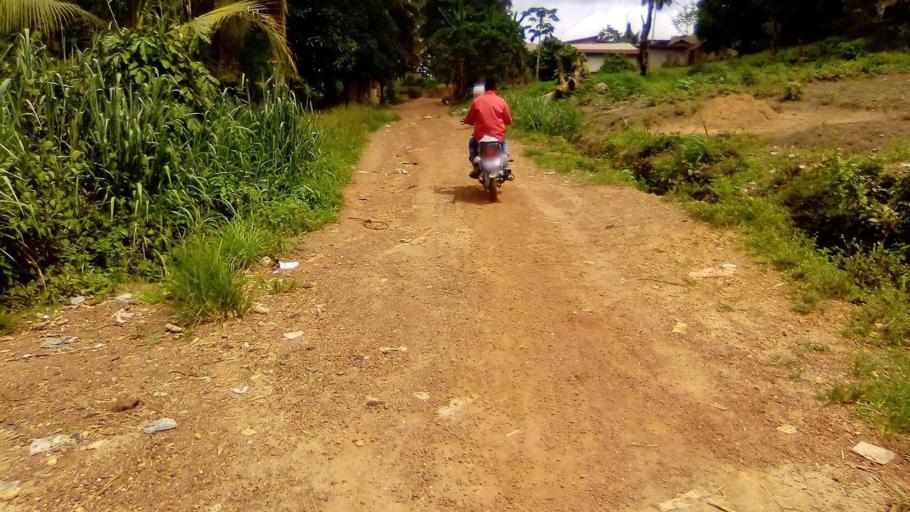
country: SL
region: Southern Province
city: Bo
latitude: 7.9629
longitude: -11.7236
